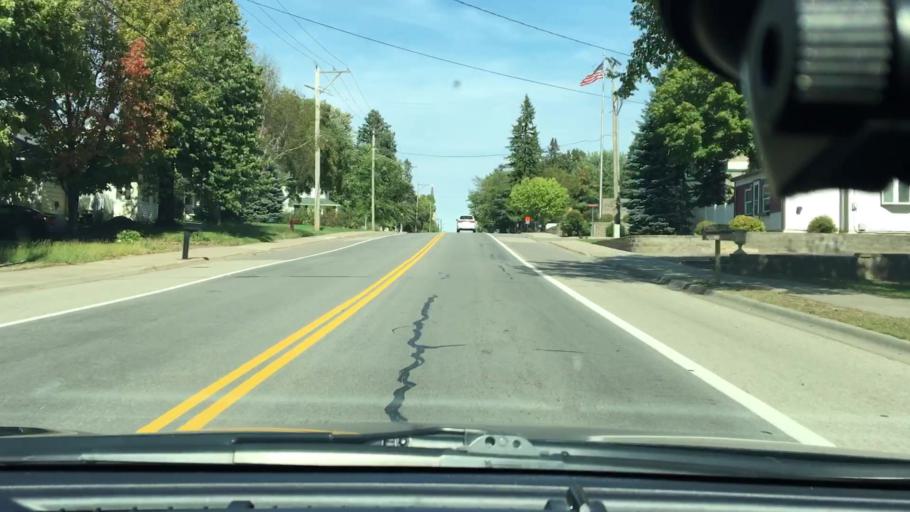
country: US
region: Minnesota
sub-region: Wright County
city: Saint Michael
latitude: 45.2053
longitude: -93.6648
